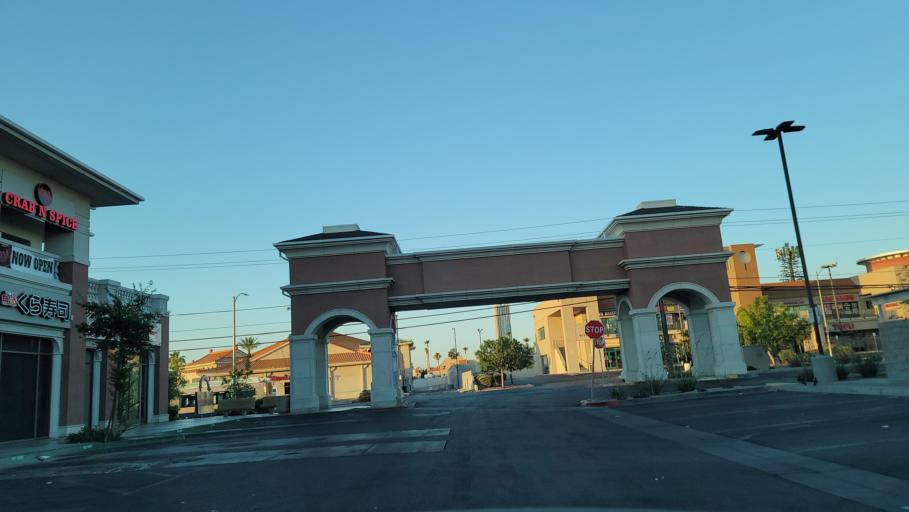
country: US
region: Nevada
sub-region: Clark County
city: Spring Valley
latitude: 36.1270
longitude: -115.1974
